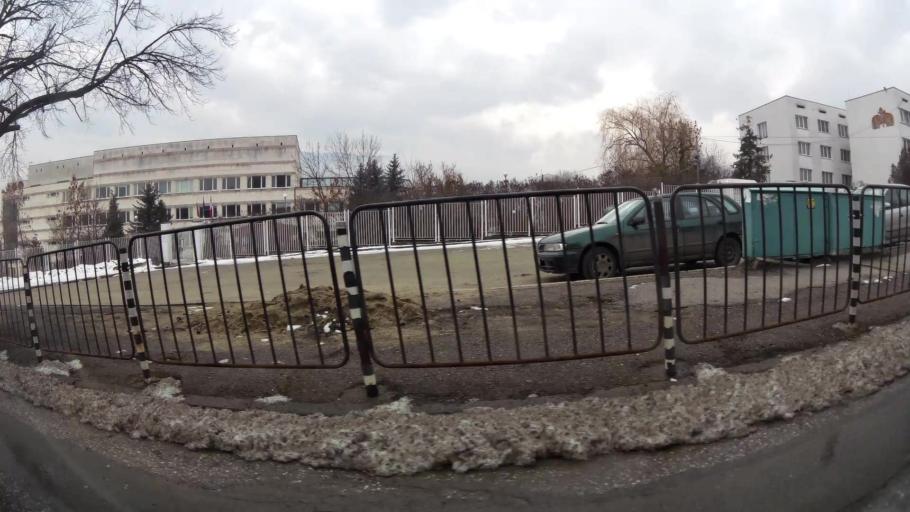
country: BG
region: Sofiya
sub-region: Obshtina Bozhurishte
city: Bozhurishte
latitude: 42.6759
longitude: 23.2321
